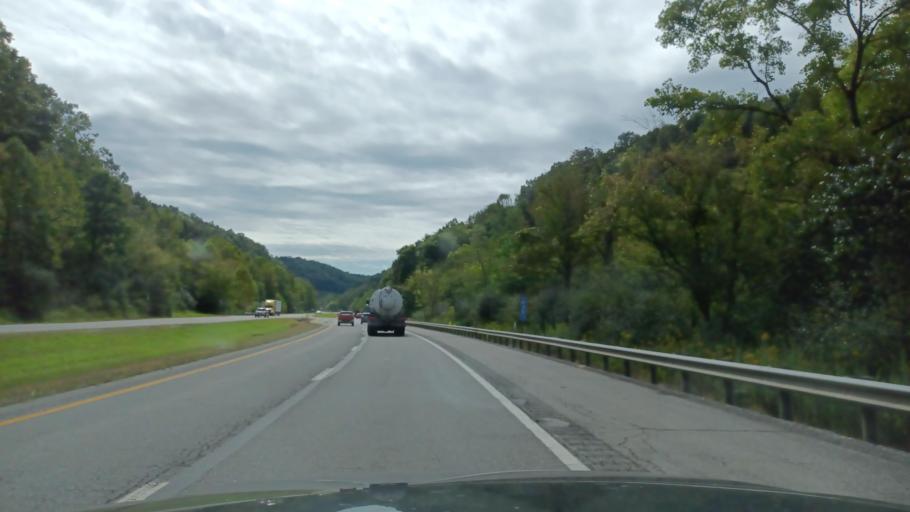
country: US
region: West Virginia
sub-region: Pleasants County
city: Saint Marys
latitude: 39.2524
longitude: -81.2010
